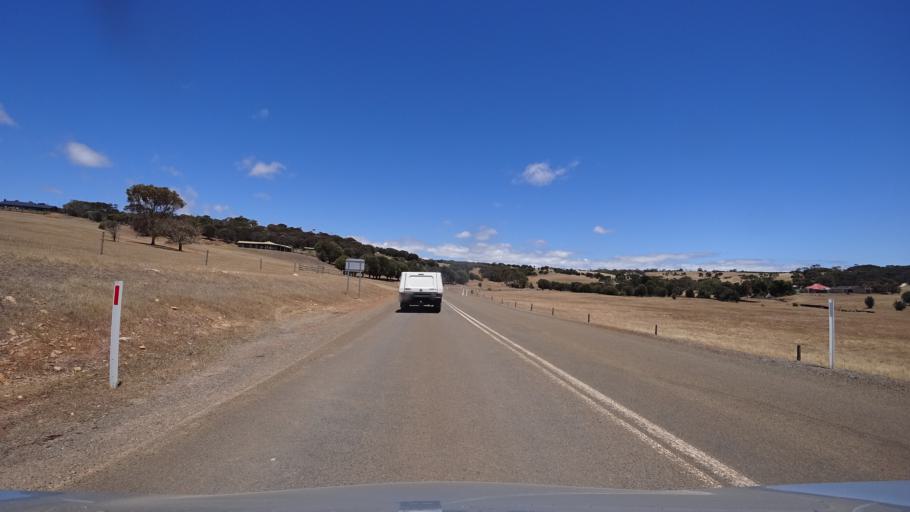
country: AU
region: South Australia
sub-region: Kangaroo Island
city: Kingscote
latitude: -35.6260
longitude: 137.2066
